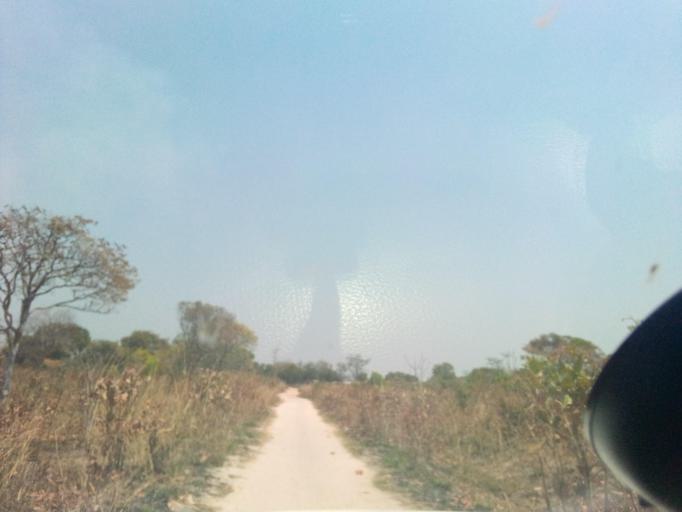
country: ZM
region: Copperbelt
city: Kataba
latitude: -12.2447
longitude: 30.3294
